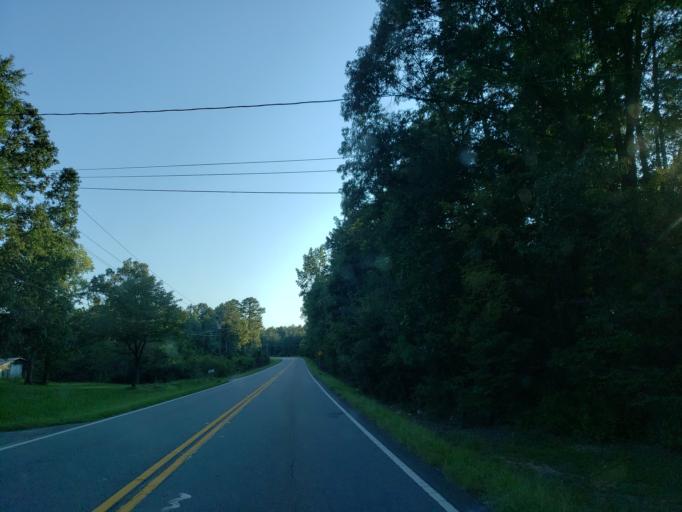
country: US
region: Georgia
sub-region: Murray County
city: Chatsworth
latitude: 34.6993
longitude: -84.8209
